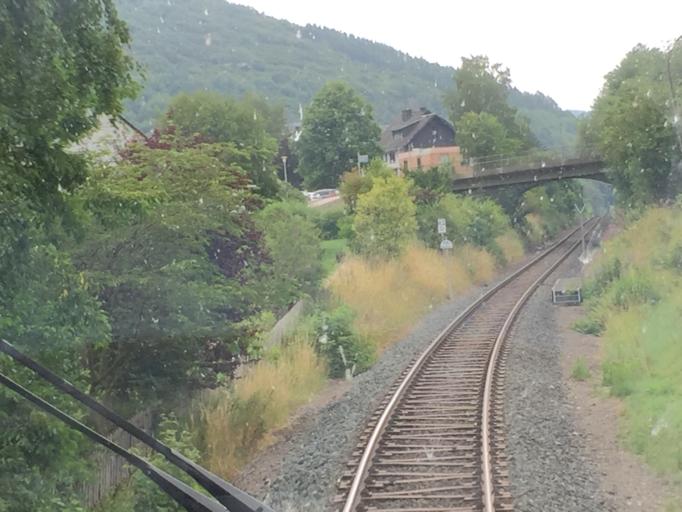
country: DE
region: Hesse
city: Willingen
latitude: 51.2925
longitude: 8.6092
